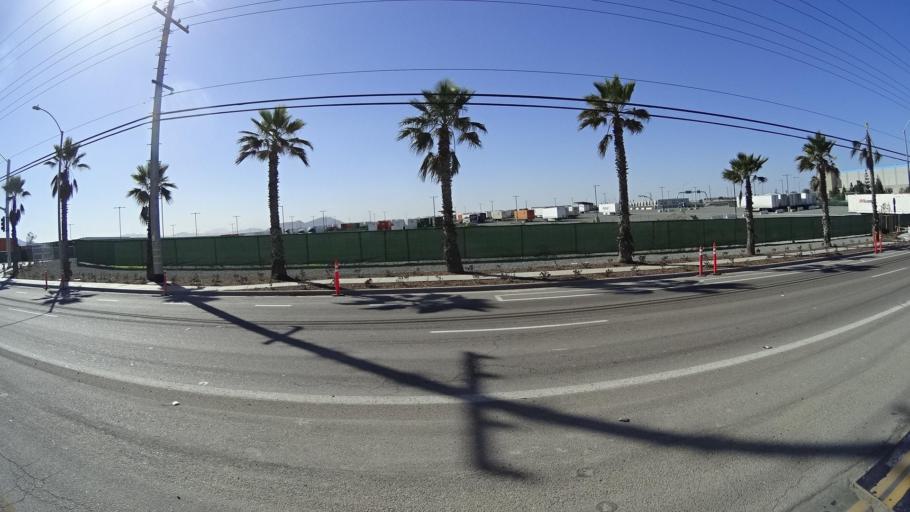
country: MX
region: Baja California
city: Tijuana
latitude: 32.5675
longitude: -116.9260
